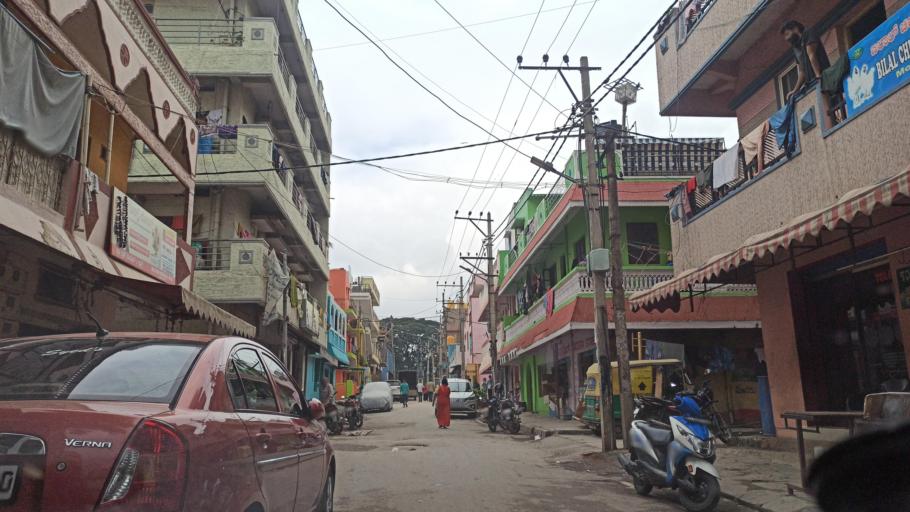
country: IN
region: Karnataka
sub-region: Bangalore Urban
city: Bangalore
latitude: 12.9990
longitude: 77.6714
